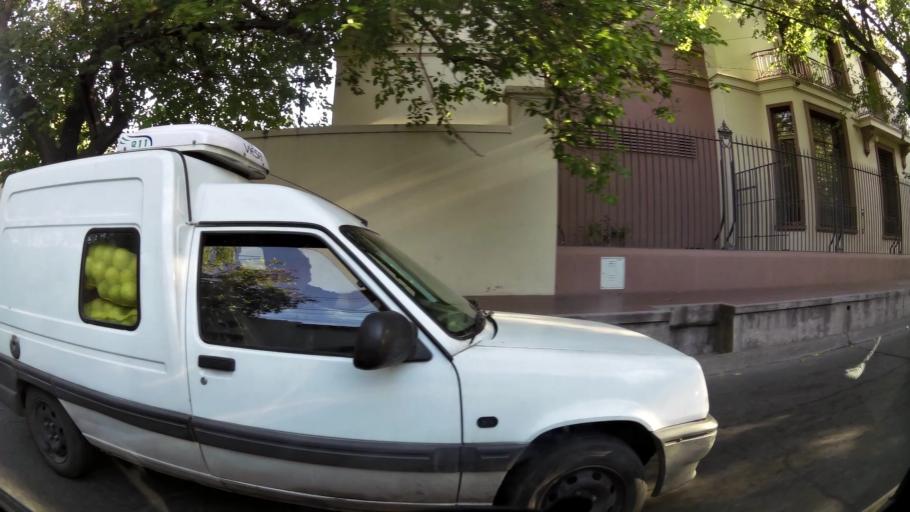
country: AR
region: Mendoza
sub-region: Departamento de Godoy Cruz
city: Godoy Cruz
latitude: -32.9121
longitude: -68.8446
